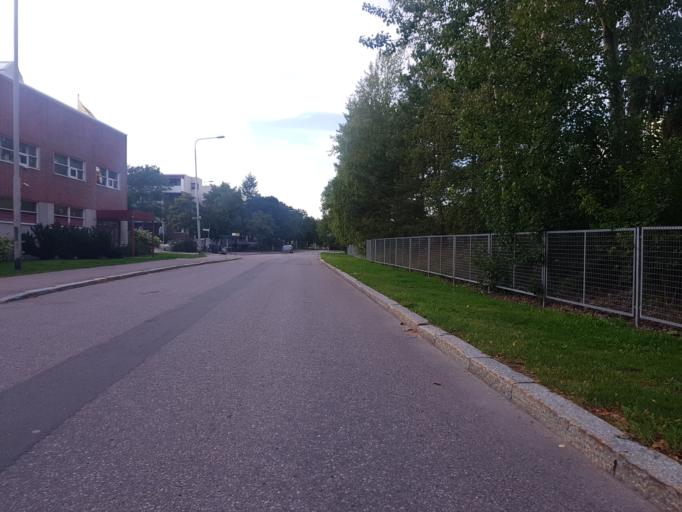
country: FI
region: Uusimaa
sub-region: Helsinki
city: Teekkarikylae
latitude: 60.2438
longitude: 24.8665
